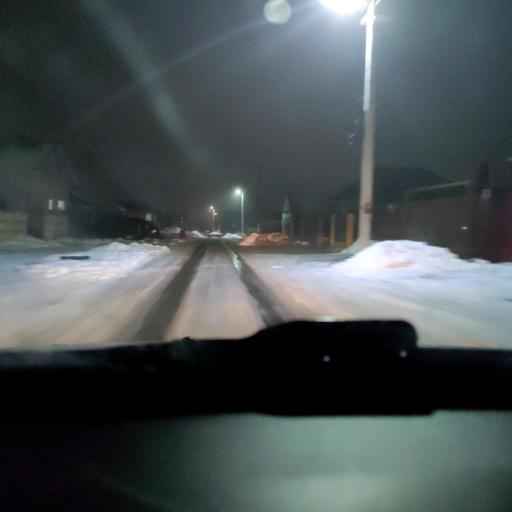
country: RU
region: Voronezj
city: Podgornoye
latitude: 51.7965
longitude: 39.1439
